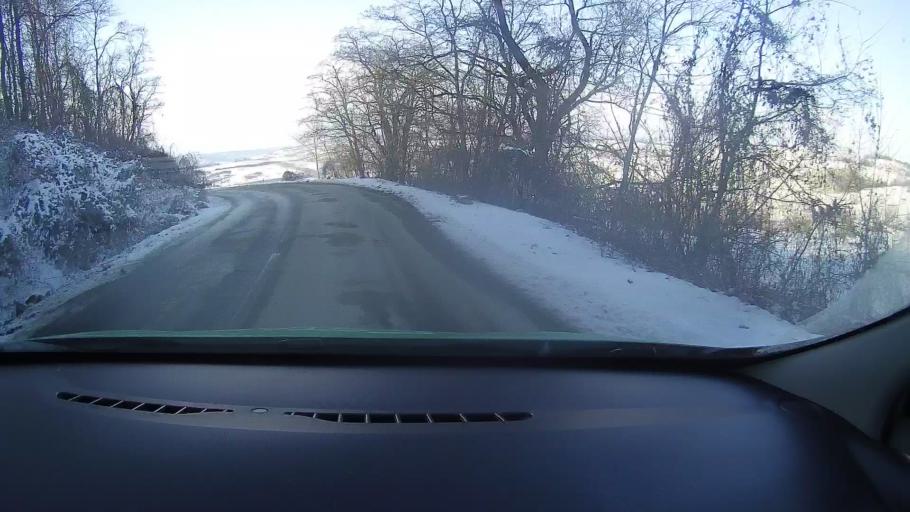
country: RO
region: Sibiu
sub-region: Oras Agnita
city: Ruja
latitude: 45.9872
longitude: 24.6802
